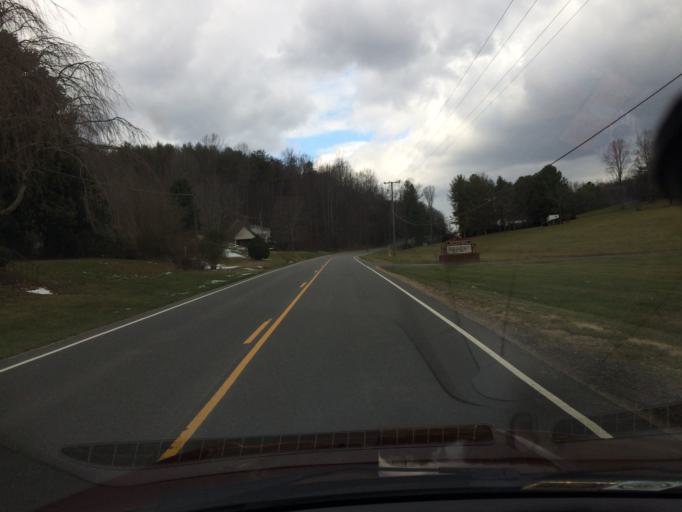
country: US
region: Virginia
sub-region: Patrick County
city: Stuart
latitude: 36.7285
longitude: -80.2428
